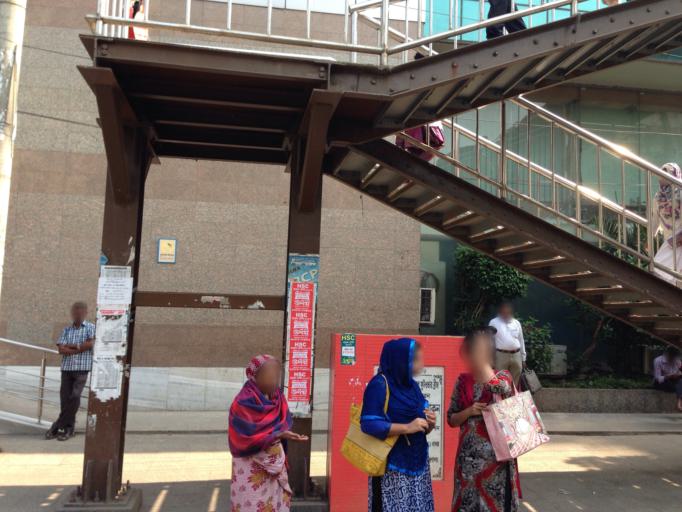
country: BD
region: Dhaka
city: Azimpur
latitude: 23.7419
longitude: 90.3829
